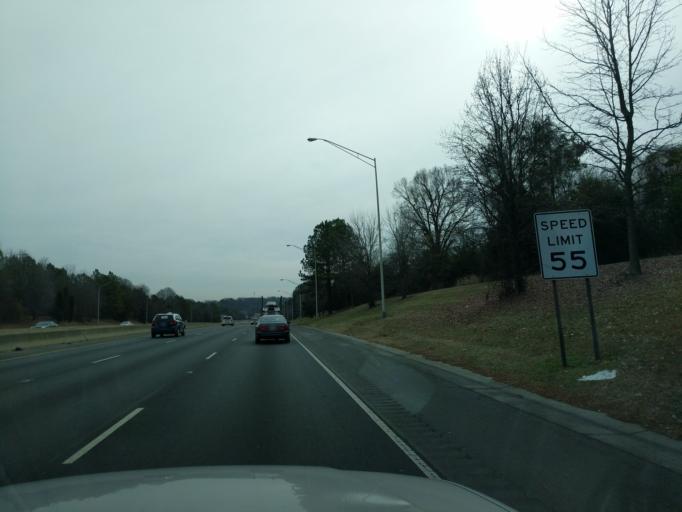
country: US
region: North Carolina
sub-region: Mecklenburg County
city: Charlotte
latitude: 35.2162
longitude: -80.8098
